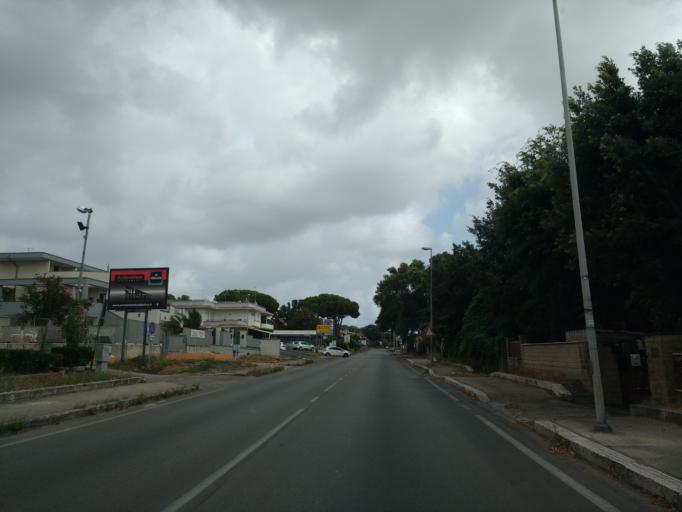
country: IT
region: Latium
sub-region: Citta metropolitana di Roma Capitale
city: Anzio
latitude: 41.4842
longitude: 12.6017
